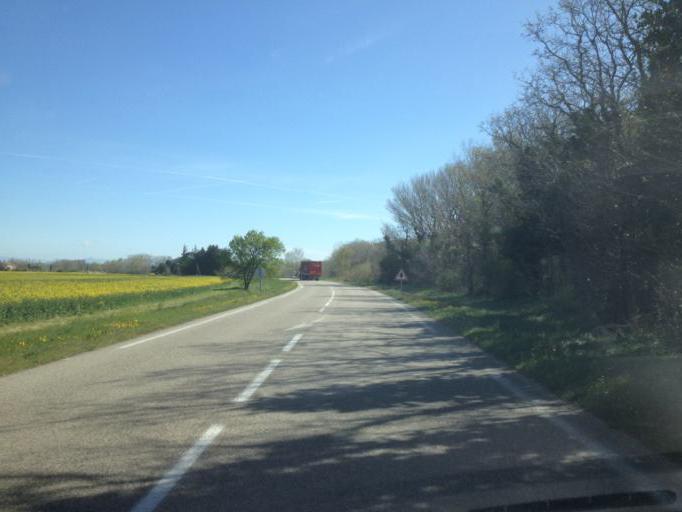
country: FR
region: Provence-Alpes-Cote d'Azur
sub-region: Departement du Vaucluse
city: Caderousse
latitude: 44.1342
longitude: 4.7387
